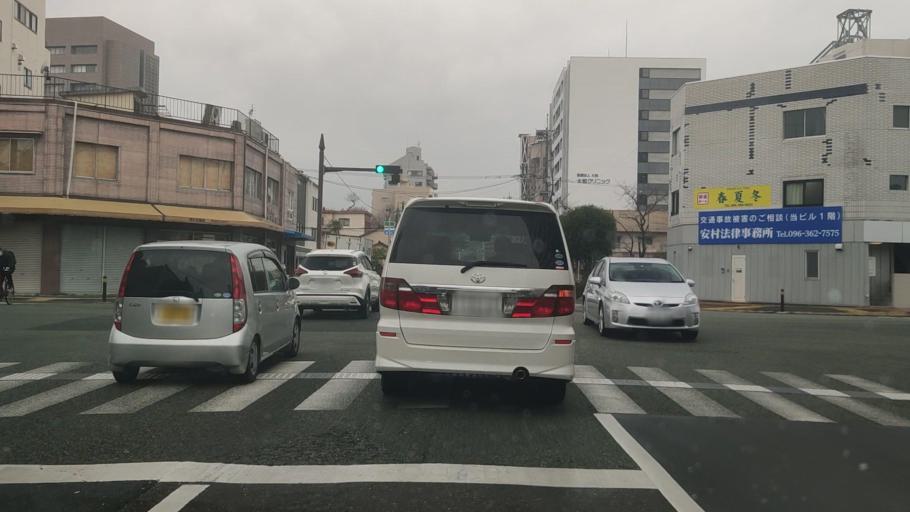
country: JP
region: Kumamoto
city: Kumamoto
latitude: 32.7968
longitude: 130.7150
